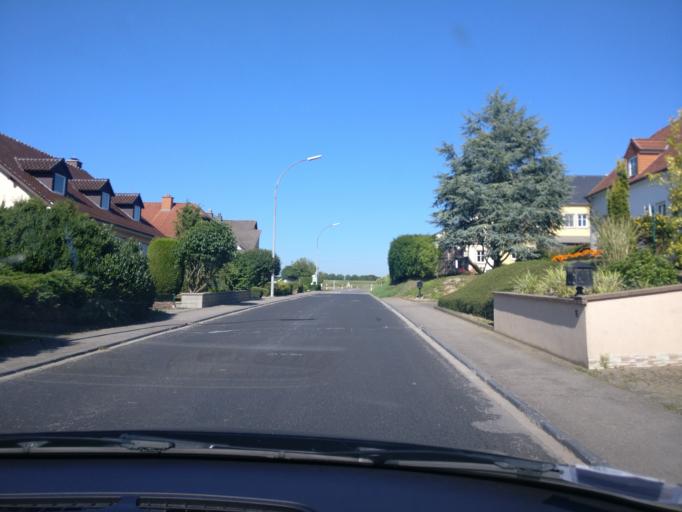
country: LU
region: Grevenmacher
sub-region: Canton de Grevenmacher
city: Betzdorf
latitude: 49.7184
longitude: 6.3124
